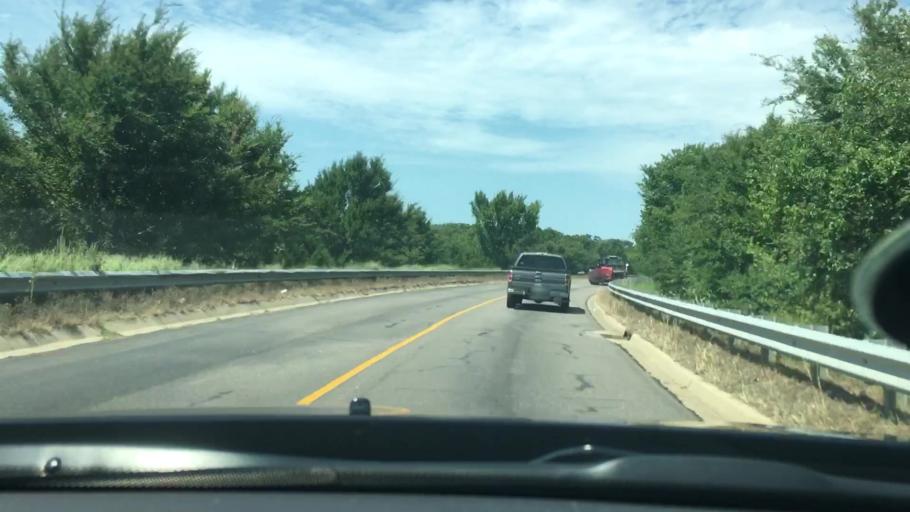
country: US
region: Oklahoma
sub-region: Pontotoc County
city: Ada
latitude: 34.7907
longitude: -96.6411
